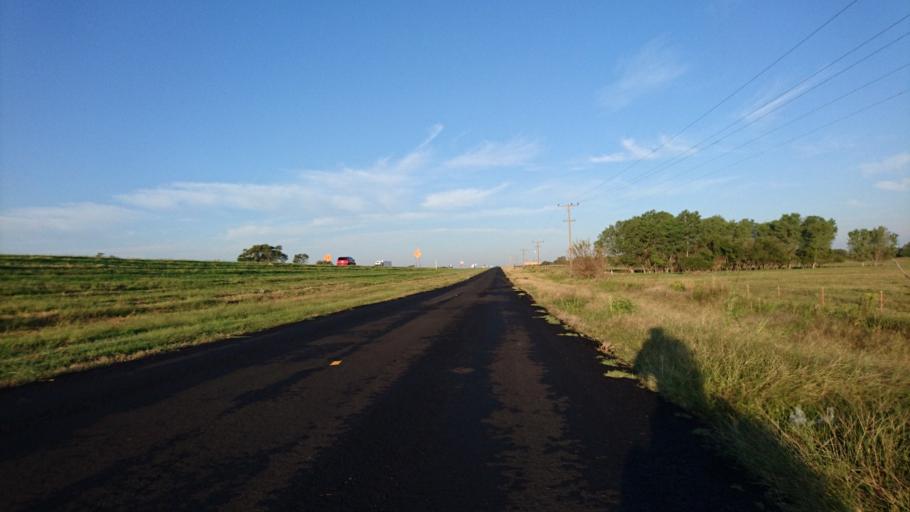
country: US
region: Oklahoma
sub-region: Beckham County
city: Sayre
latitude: 35.2624
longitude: -99.6909
